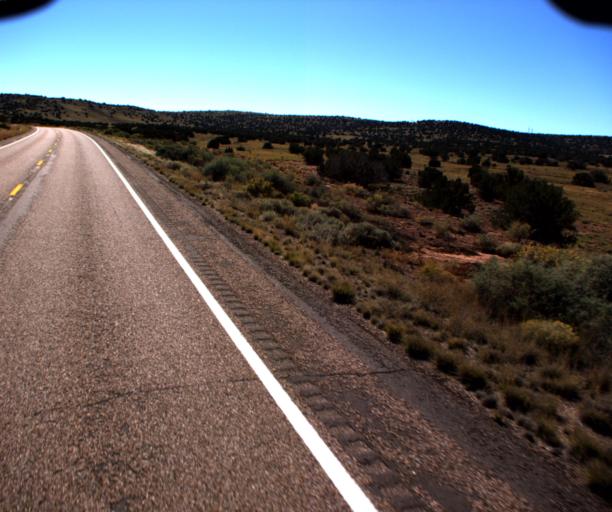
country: US
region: Arizona
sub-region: Apache County
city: Saint Johns
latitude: 34.5755
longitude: -109.5301
